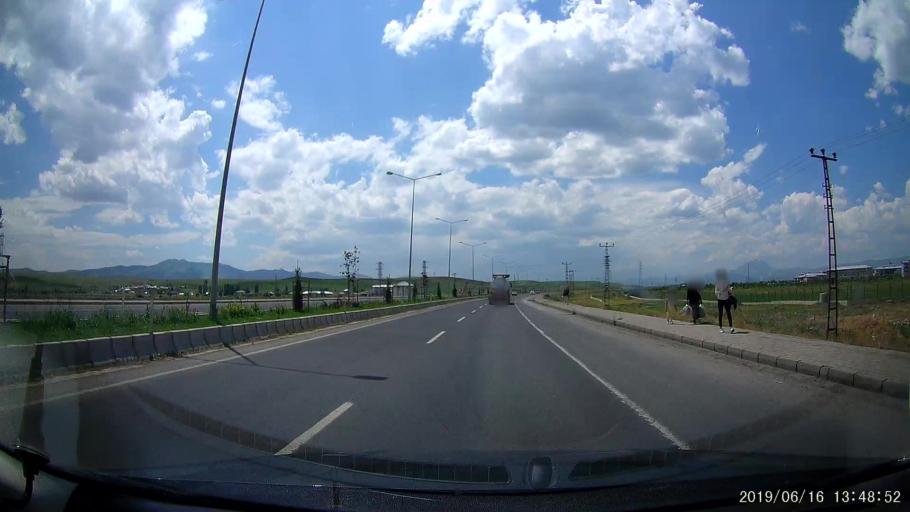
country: TR
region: Agri
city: Agri
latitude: 39.7148
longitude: 42.9996
